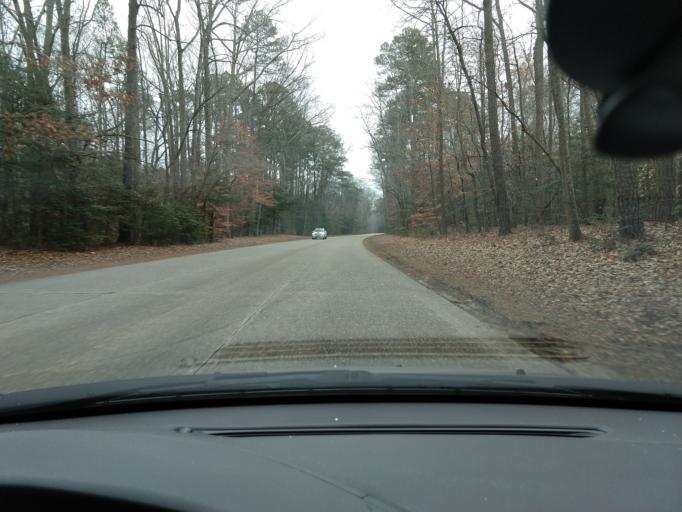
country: US
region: Virginia
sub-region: City of Williamsburg
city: Williamsburg
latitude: 37.2829
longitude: -76.6365
